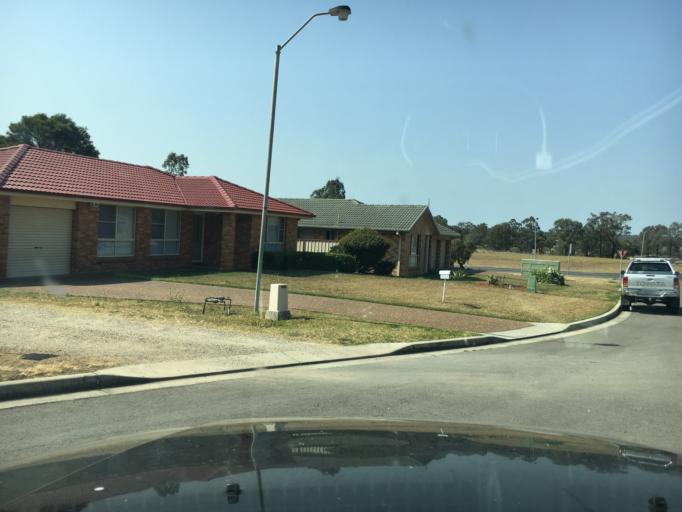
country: AU
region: New South Wales
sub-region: Singleton
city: Singleton
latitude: -32.5560
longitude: 151.1570
